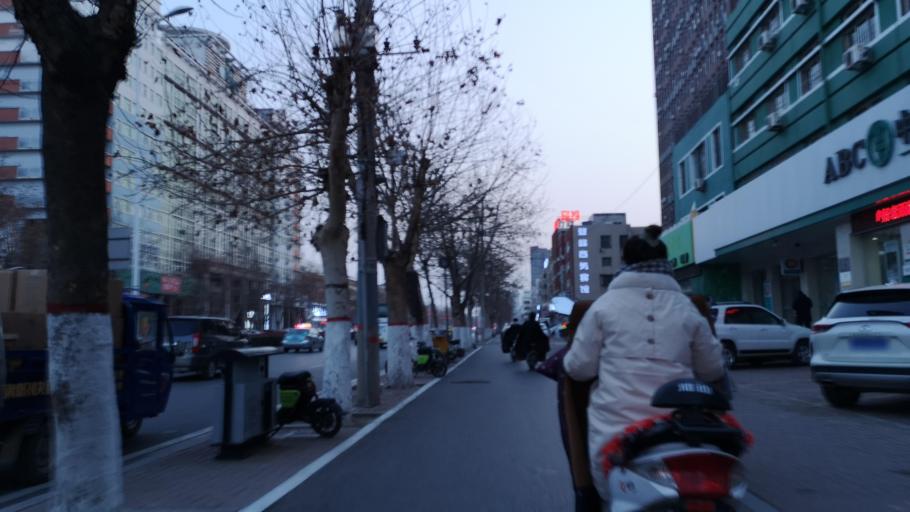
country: CN
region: Henan Sheng
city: Zhongyuanlu
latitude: 35.7686
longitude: 115.0689
